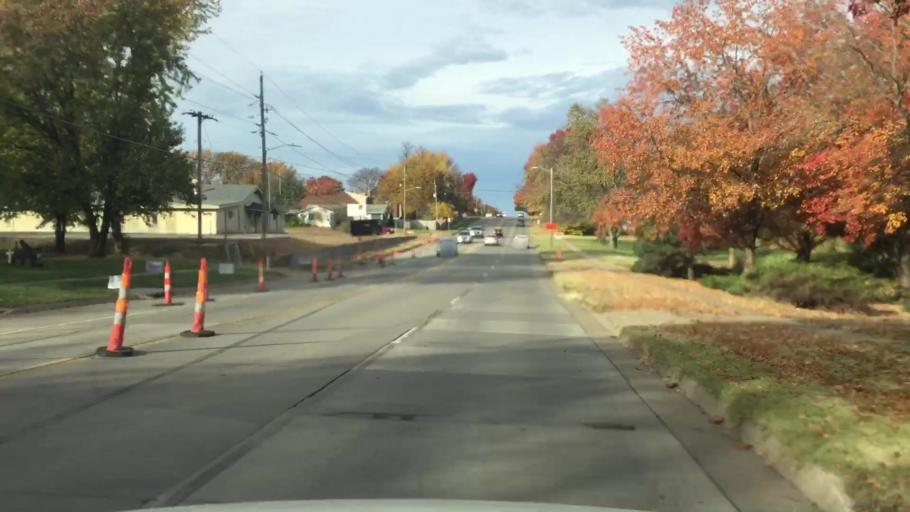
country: US
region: Kansas
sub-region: Shawnee County
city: Topeka
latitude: 39.0152
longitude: -95.6997
